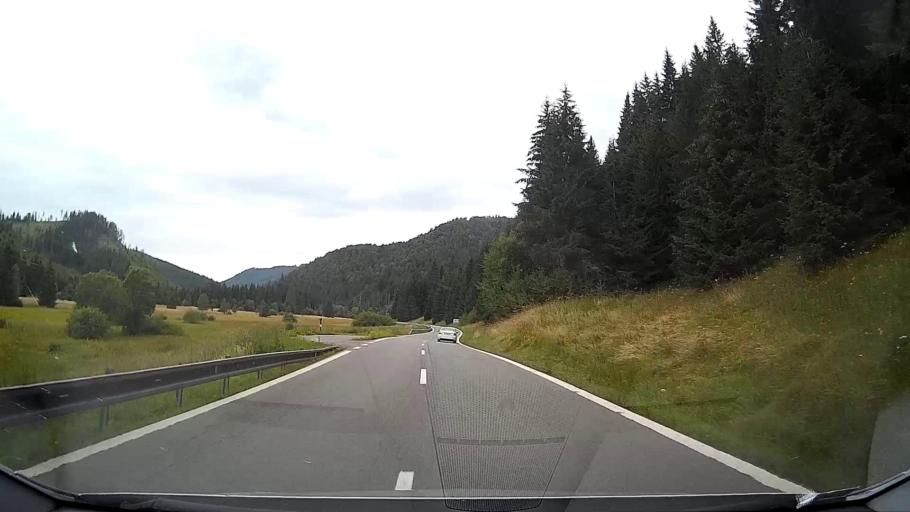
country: SK
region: Banskobystricky
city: Revuca
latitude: 48.8277
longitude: 20.1564
